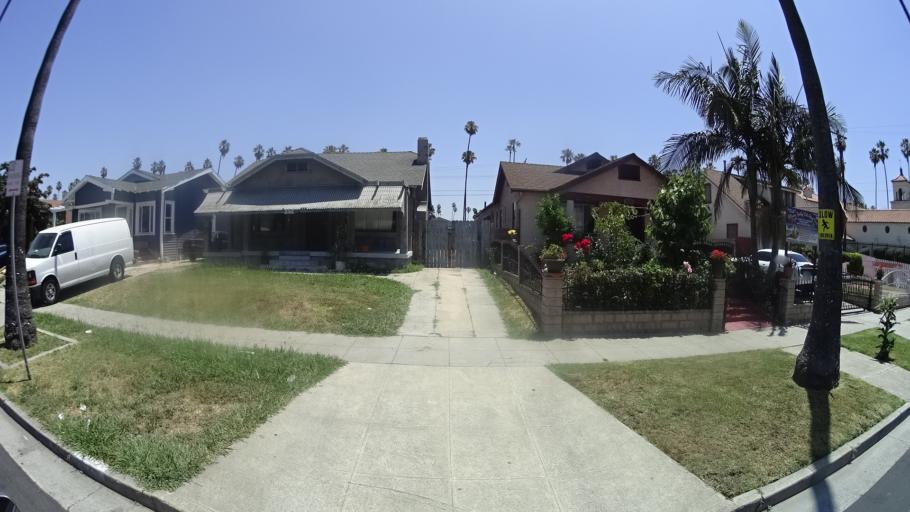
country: US
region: California
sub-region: Los Angeles County
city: View Park-Windsor Hills
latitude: 33.9939
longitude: -118.3138
